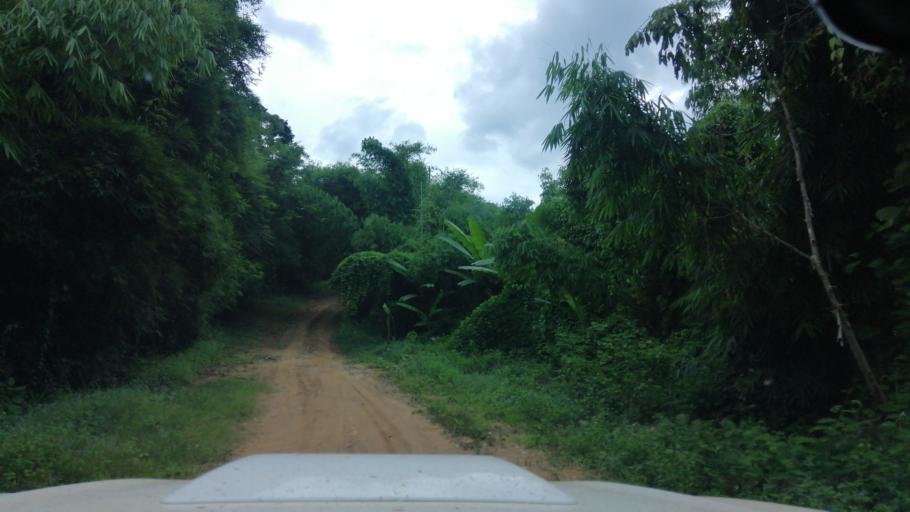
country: TH
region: Nan
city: Mae Charim
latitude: 18.7536
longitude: 101.2900
